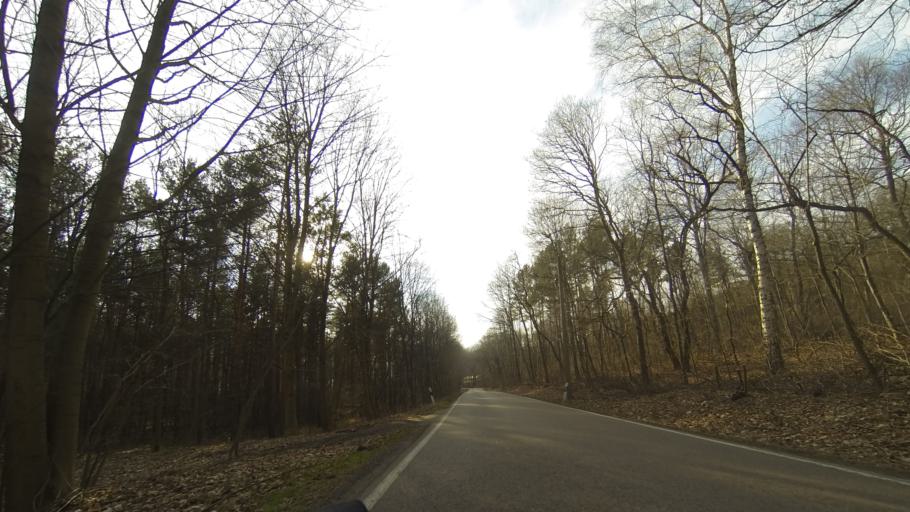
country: DE
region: Saxony
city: Radebeul
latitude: 51.1115
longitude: 13.6969
